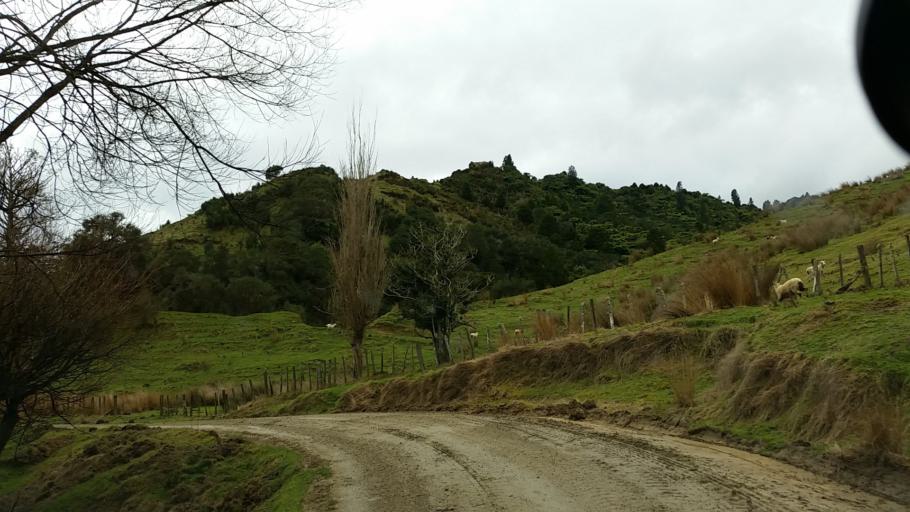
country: NZ
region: Taranaki
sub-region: South Taranaki District
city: Patea
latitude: -39.6564
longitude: 174.7525
